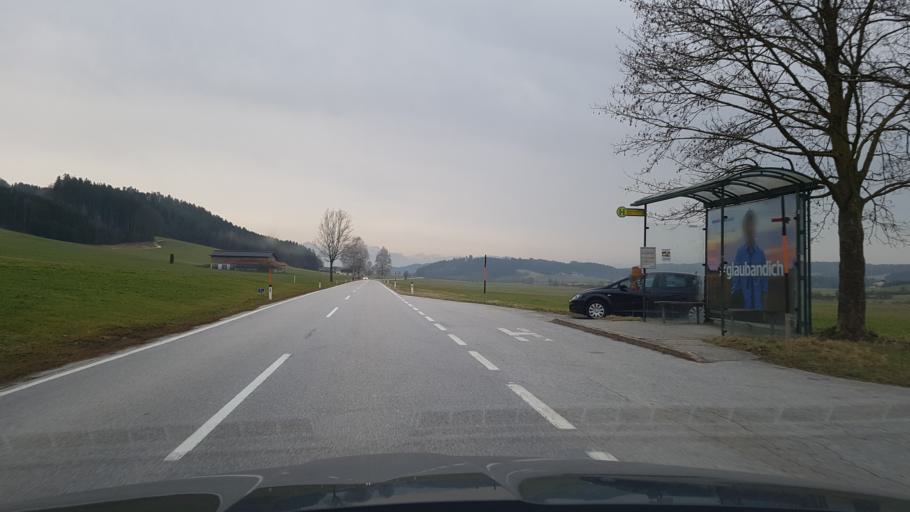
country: AT
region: Salzburg
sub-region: Politischer Bezirk Salzburg-Umgebung
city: Dorfbeuern
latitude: 47.9940
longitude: 13.0226
